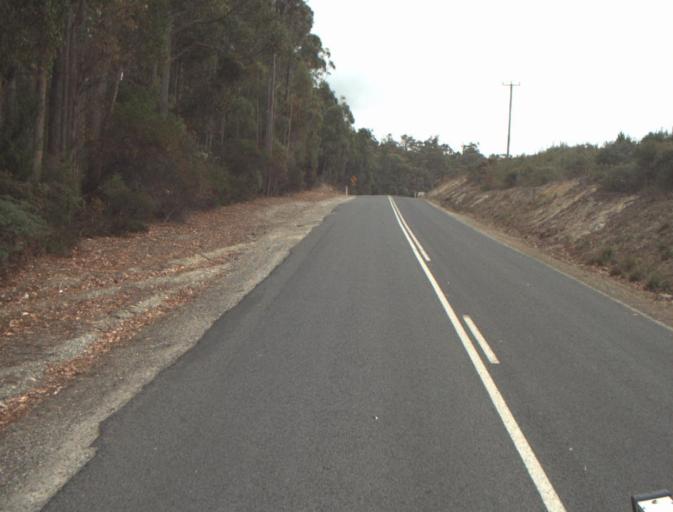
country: AU
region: Tasmania
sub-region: Dorset
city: Bridport
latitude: -41.1678
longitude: 147.2622
